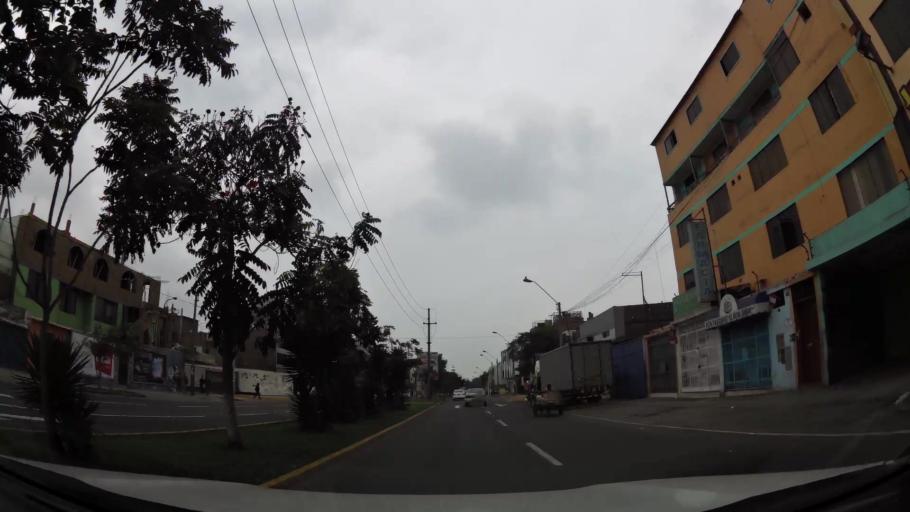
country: PE
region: Lima
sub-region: Lima
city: San Luis
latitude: -12.0764
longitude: -76.9957
